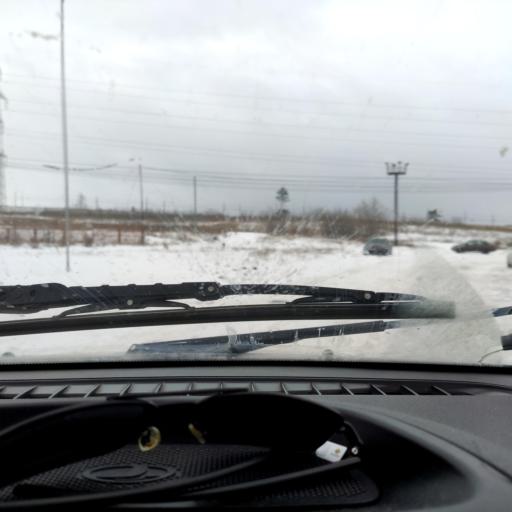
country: RU
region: Samara
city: Zhigulevsk
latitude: 53.5157
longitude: 49.5273
